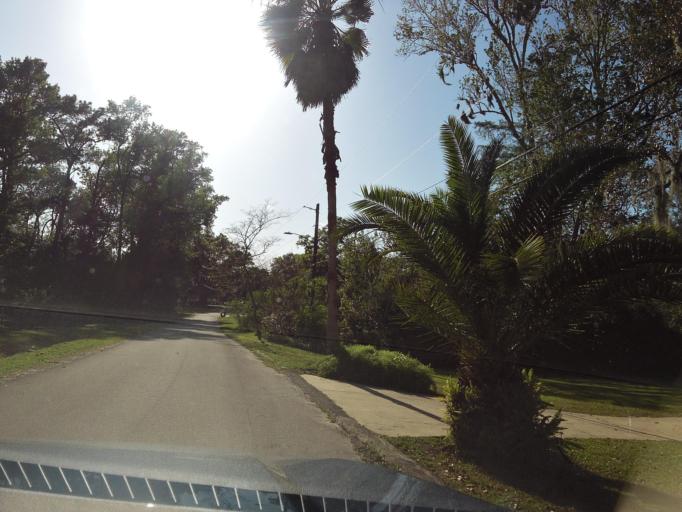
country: US
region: Florida
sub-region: Duval County
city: Jacksonville
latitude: 30.2780
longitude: -81.5730
